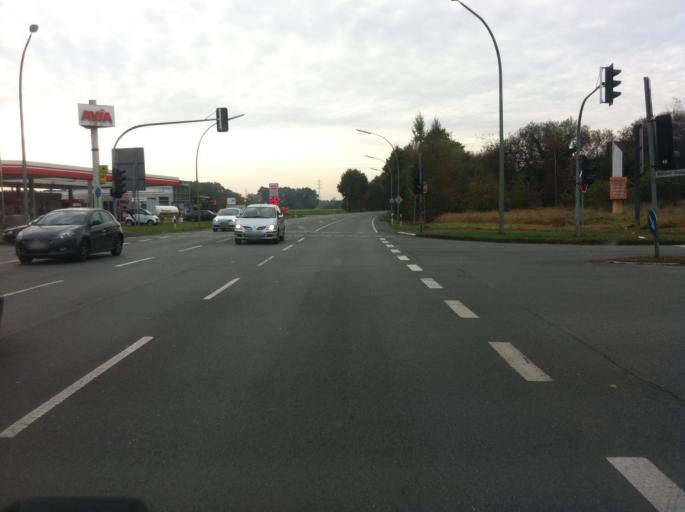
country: DE
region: North Rhine-Westphalia
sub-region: Regierungsbezirk Munster
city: Vreden
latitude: 52.0347
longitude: 6.8412
